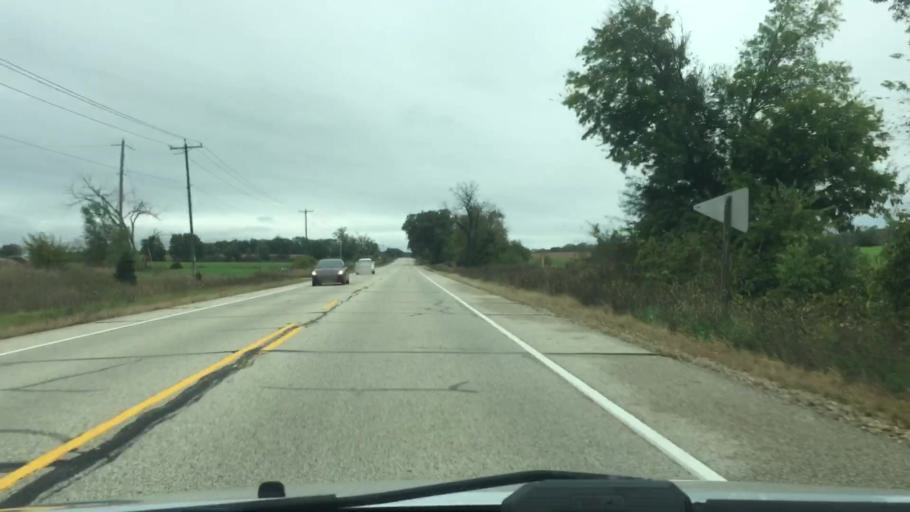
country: US
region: Wisconsin
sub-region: Jefferson County
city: Palmyra
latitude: 42.8333
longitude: -88.5453
